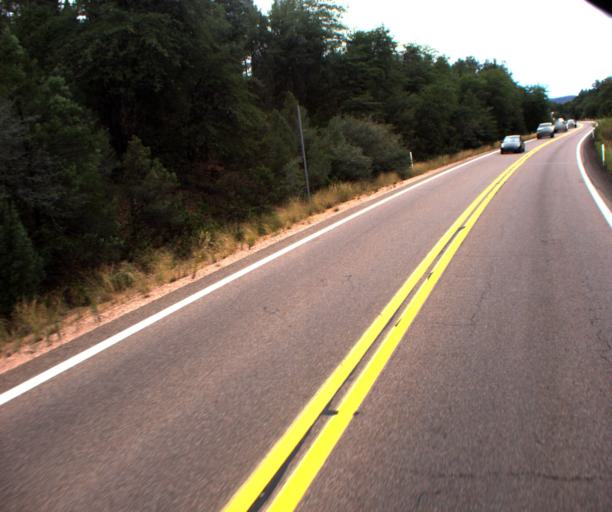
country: US
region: Arizona
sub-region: Gila County
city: Star Valley
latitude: 34.2604
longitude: -111.2506
